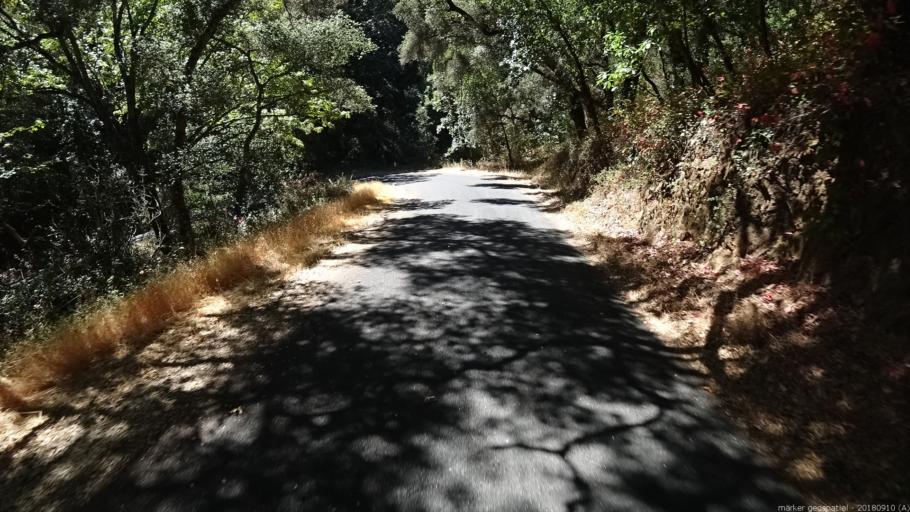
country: US
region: California
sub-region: Monterey County
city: Carmel Valley Village
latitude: 36.4296
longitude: -121.7913
